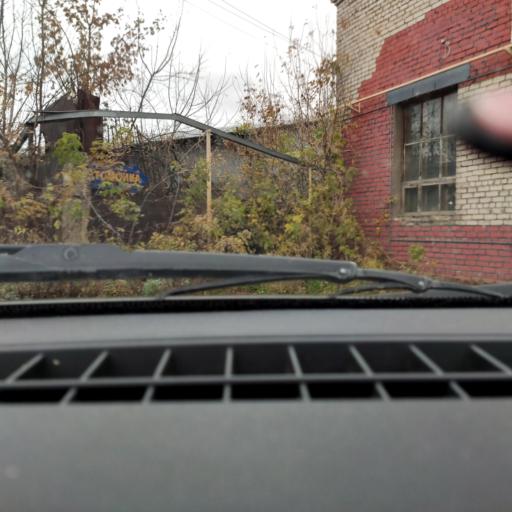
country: RU
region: Bashkortostan
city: Ufa
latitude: 54.7829
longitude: 56.0660
